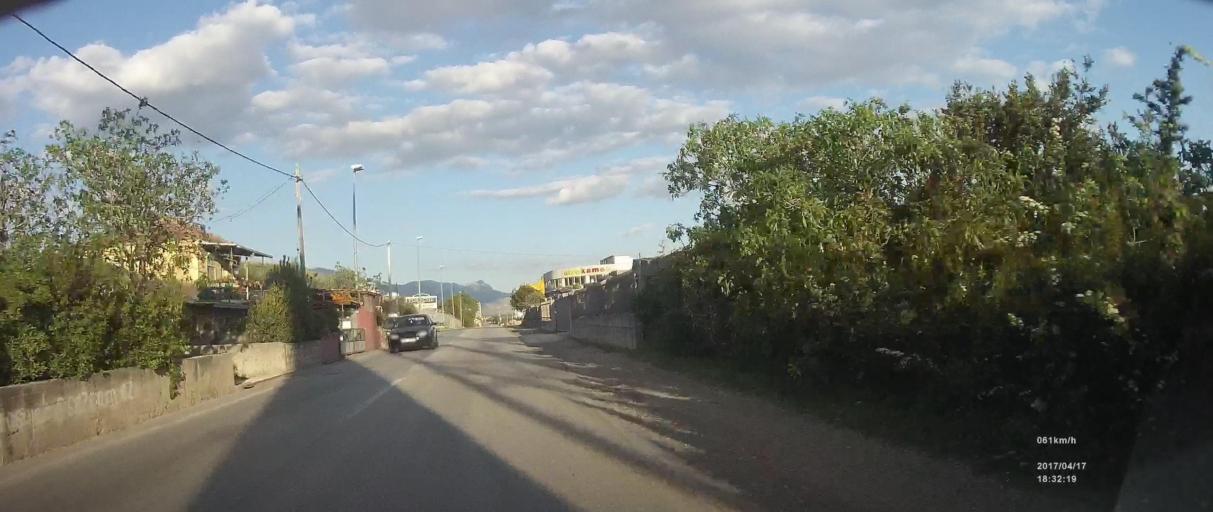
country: HR
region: Splitsko-Dalmatinska
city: Vranjic
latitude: 43.5428
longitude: 16.4444
